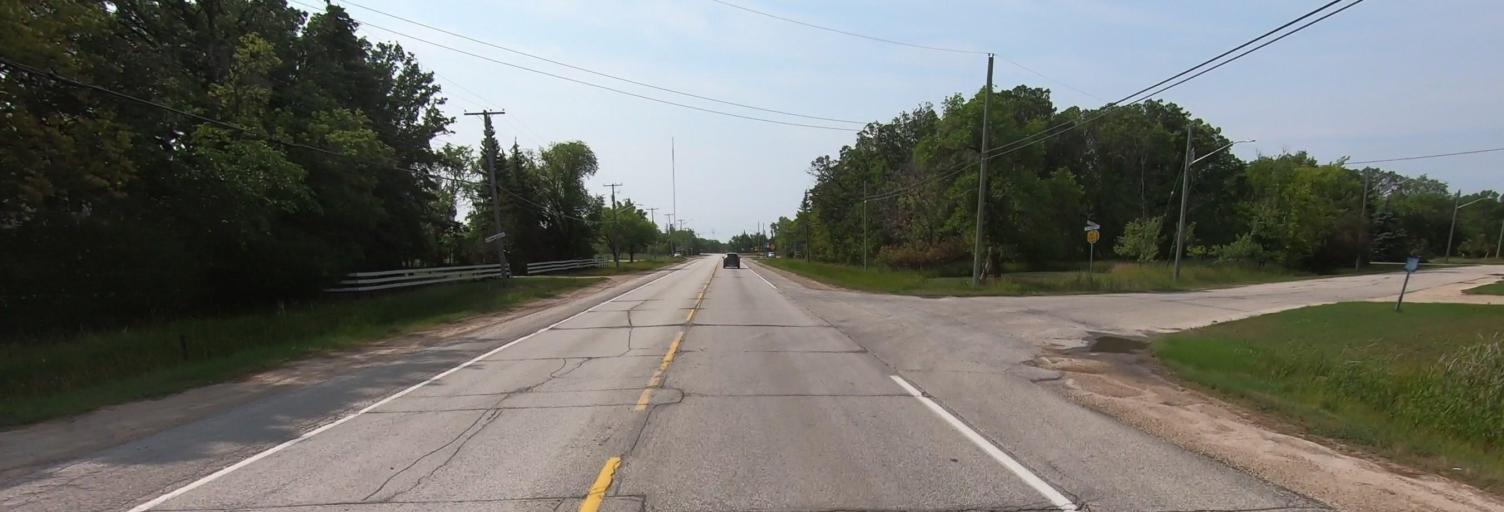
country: CA
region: Manitoba
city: Winnipeg
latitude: 49.7716
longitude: -97.1276
